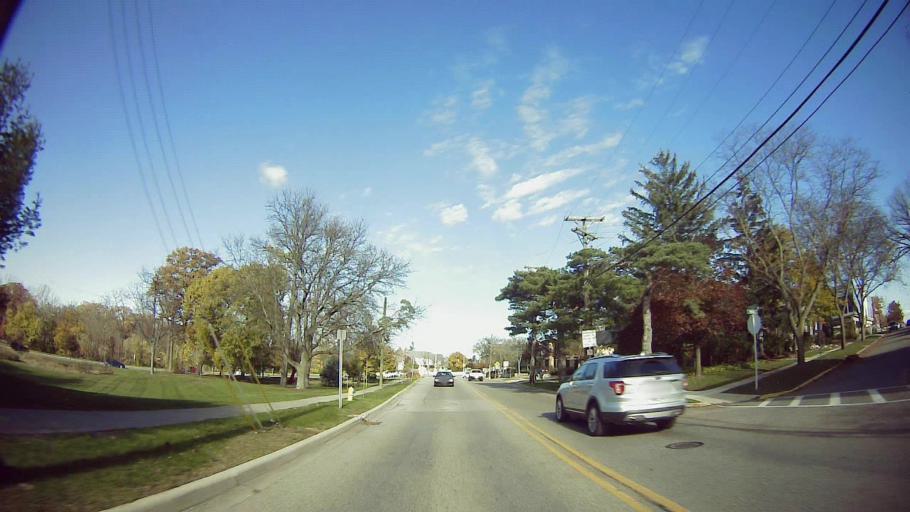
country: US
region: Michigan
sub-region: Oakland County
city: Birmingham
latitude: 42.5450
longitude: -83.2209
